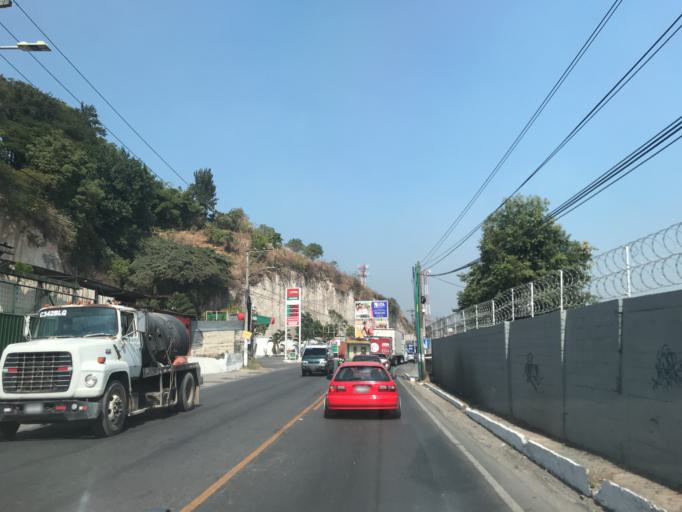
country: GT
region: Guatemala
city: Petapa
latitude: 14.5138
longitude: -90.5642
